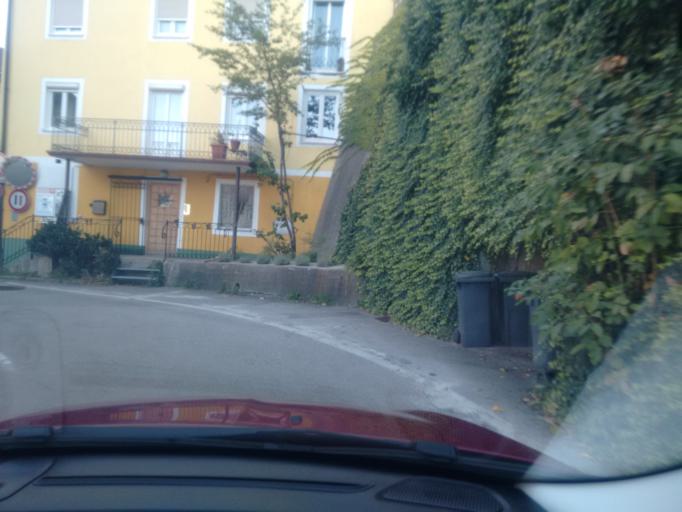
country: DE
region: Bavaria
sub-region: Upper Bavaria
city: Burghausen
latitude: 48.1576
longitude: 12.8352
